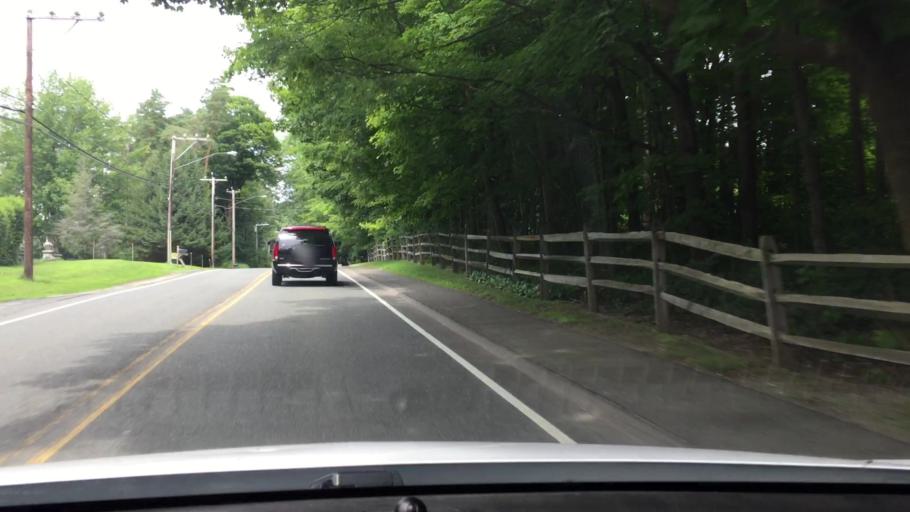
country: US
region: Massachusetts
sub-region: Berkshire County
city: Pittsfield
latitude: 42.4212
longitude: -73.2454
